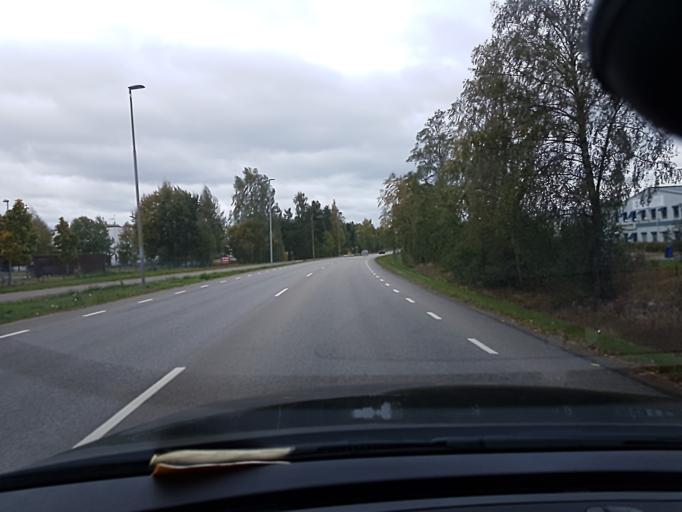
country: SE
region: Kronoberg
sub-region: Vaxjo Kommun
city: Vaexjoe
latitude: 56.9050
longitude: 14.8237
